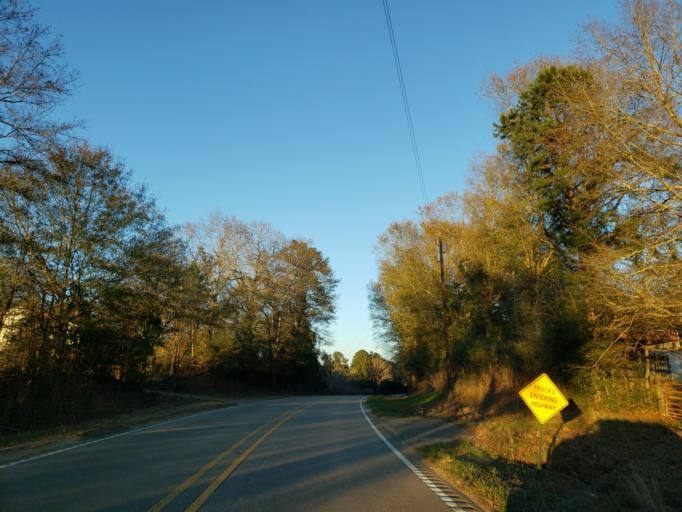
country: US
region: Mississippi
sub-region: Covington County
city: Collins
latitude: 31.5603
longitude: -89.4435
